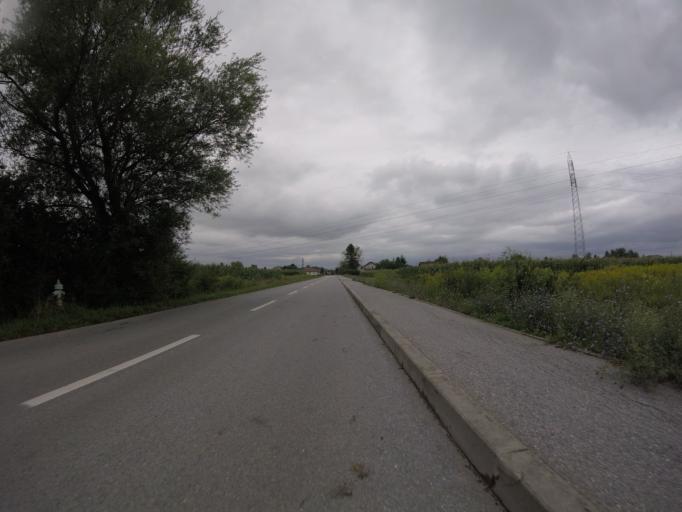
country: HR
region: Zagrebacka
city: Turopolje
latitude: 45.6313
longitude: 16.1112
